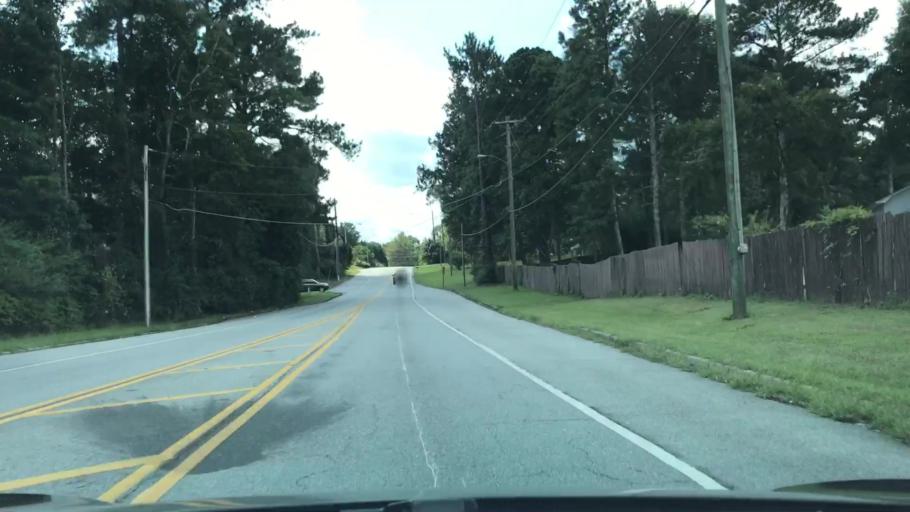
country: US
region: Georgia
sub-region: Gwinnett County
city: Lawrenceville
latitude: 33.9358
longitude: -84.0586
